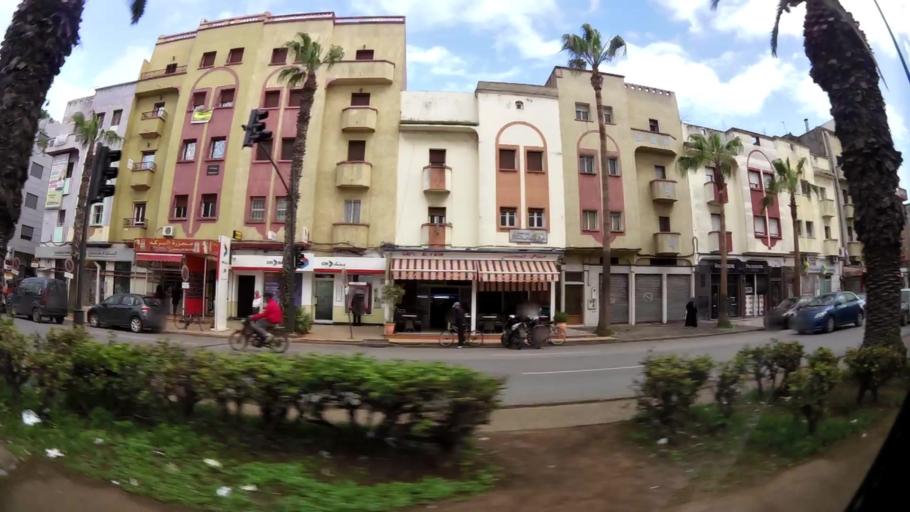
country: MA
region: Grand Casablanca
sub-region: Mohammedia
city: Mohammedia
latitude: 33.6787
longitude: -7.3919
